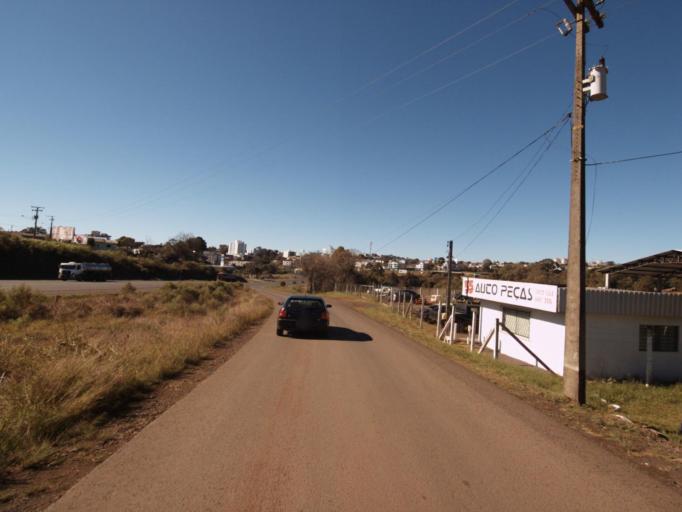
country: BR
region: Santa Catarina
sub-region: Xanxere
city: Xanxere
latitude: -26.8842
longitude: -52.4076
